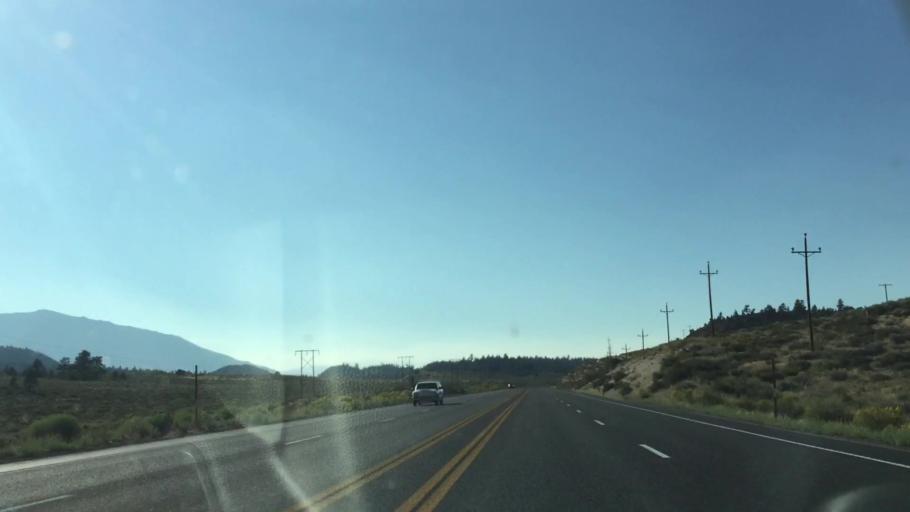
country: US
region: California
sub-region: Inyo County
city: West Bishop
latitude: 37.5535
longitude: -118.6447
